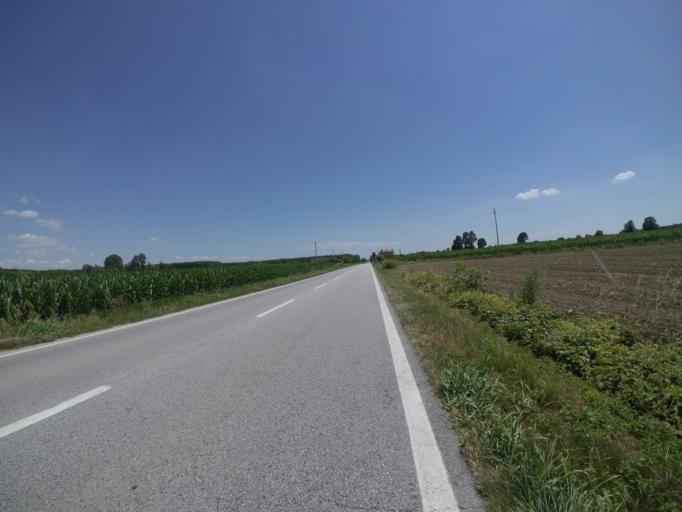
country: IT
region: Friuli Venezia Giulia
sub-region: Provincia di Udine
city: Rivignano
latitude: 45.8820
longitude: 13.0165
